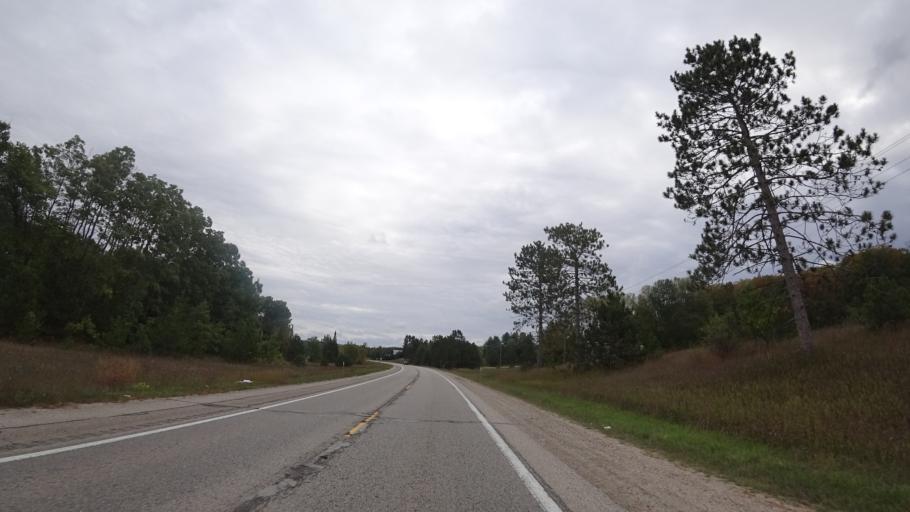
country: US
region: Michigan
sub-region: Charlevoix County
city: Boyne City
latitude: 45.2023
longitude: -84.9245
